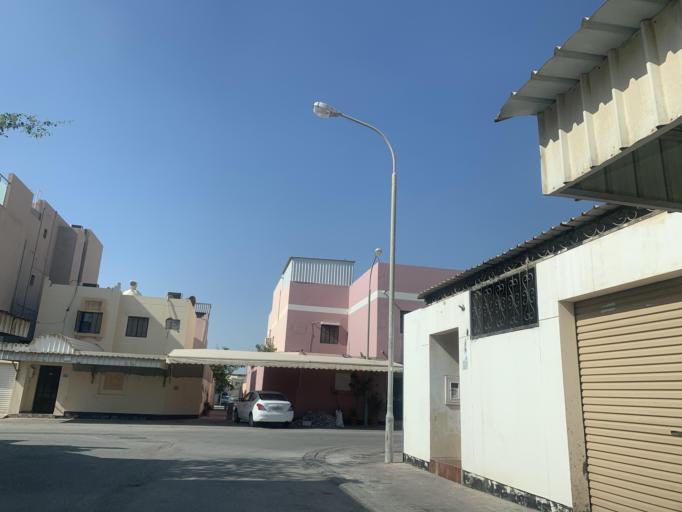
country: BH
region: Central Governorate
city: Madinat Hamad
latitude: 26.1165
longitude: 50.4979
